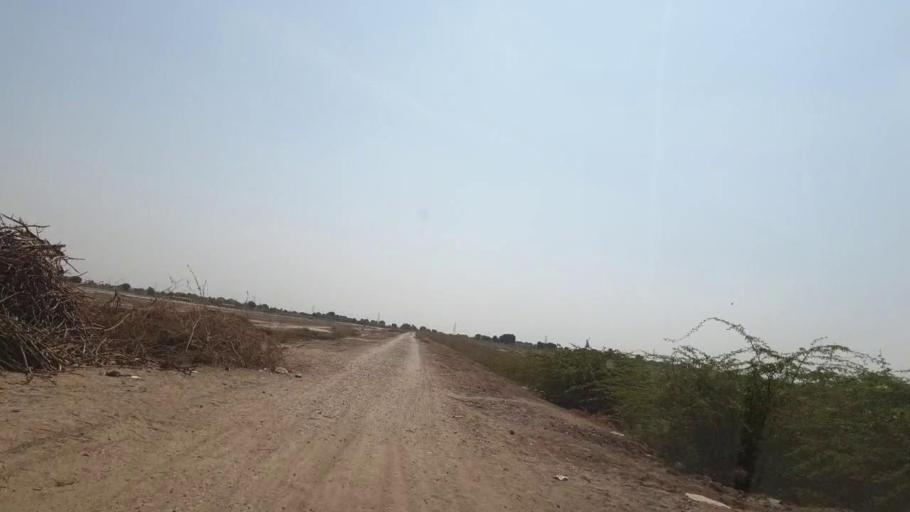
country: PK
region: Sindh
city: Nabisar
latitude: 25.0749
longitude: 69.5527
